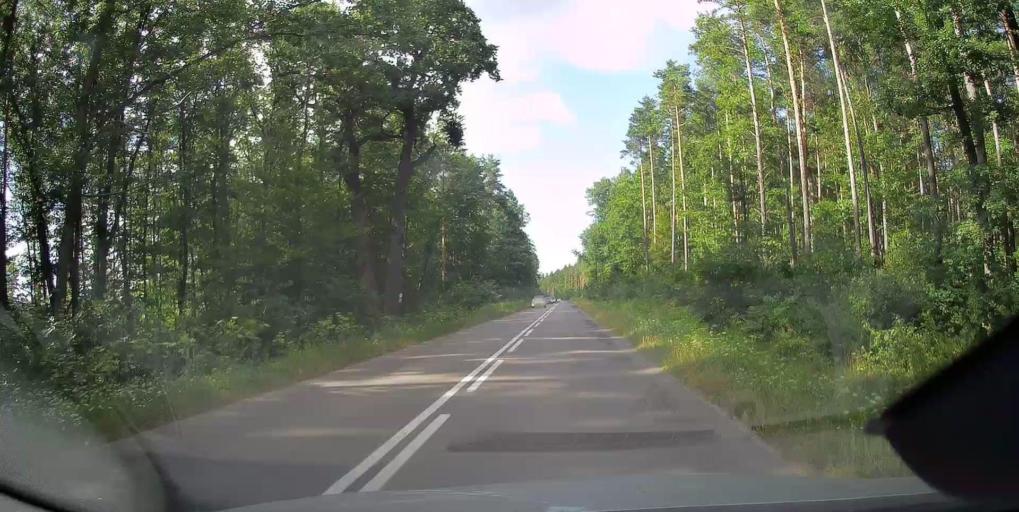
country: PL
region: Swietokrzyskie
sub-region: Powiat skarzyski
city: Suchedniow
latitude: 51.0136
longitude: 20.8400
